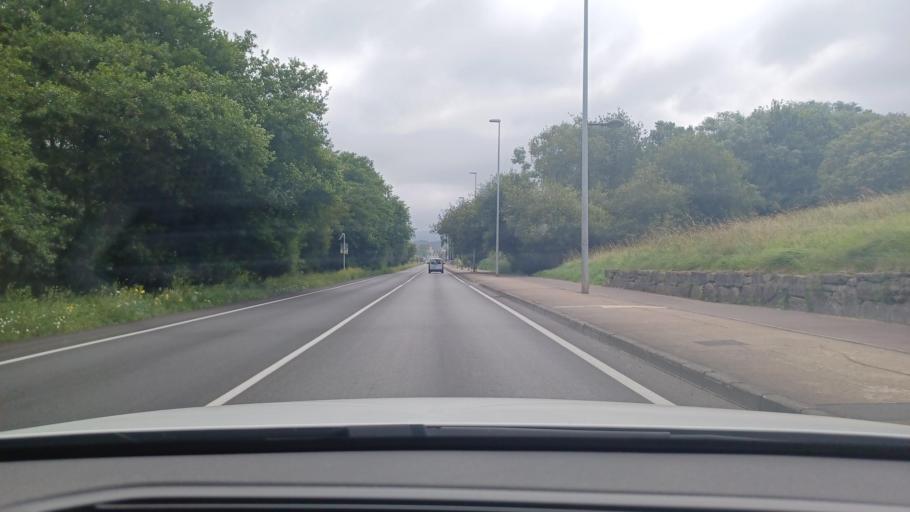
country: ES
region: Asturias
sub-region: Province of Asturias
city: Castrillon
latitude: 43.5695
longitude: -5.9624
